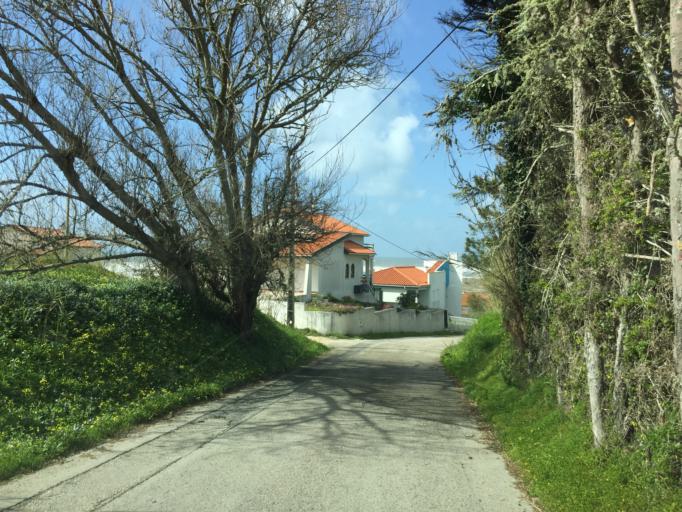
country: PT
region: Coimbra
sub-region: Figueira da Foz
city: Buarcos
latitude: 40.2074
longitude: -8.8946
